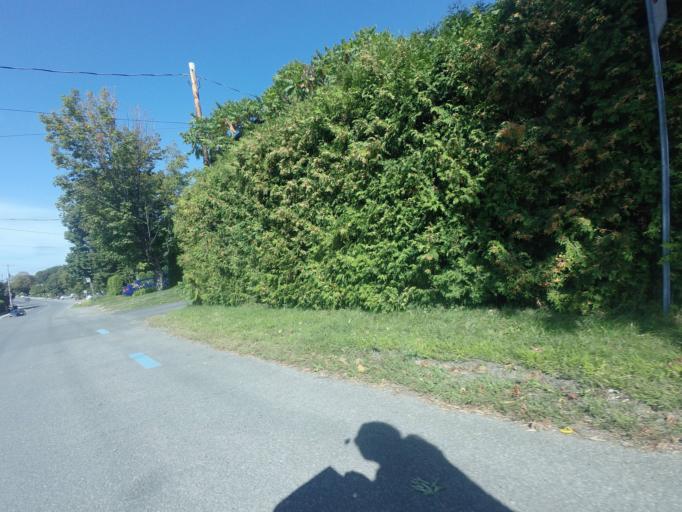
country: CA
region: Quebec
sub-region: Laurentides
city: Deux-Montagnes
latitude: 45.5374
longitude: -73.8862
